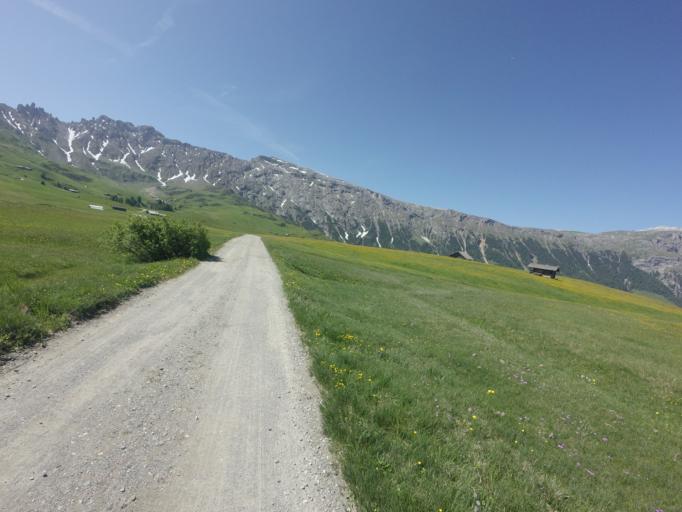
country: IT
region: Trentino-Alto Adige
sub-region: Bolzano
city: Siusi
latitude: 46.5227
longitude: 11.6245
